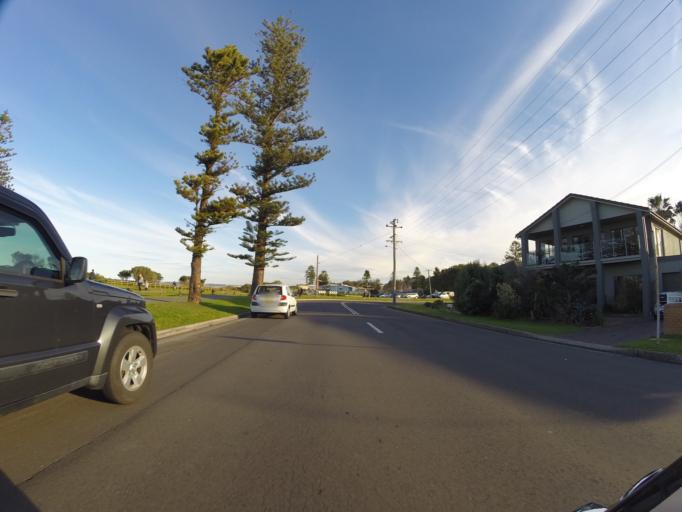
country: AU
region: New South Wales
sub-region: Wollongong
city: Bulli
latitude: -34.3395
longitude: 150.9244
